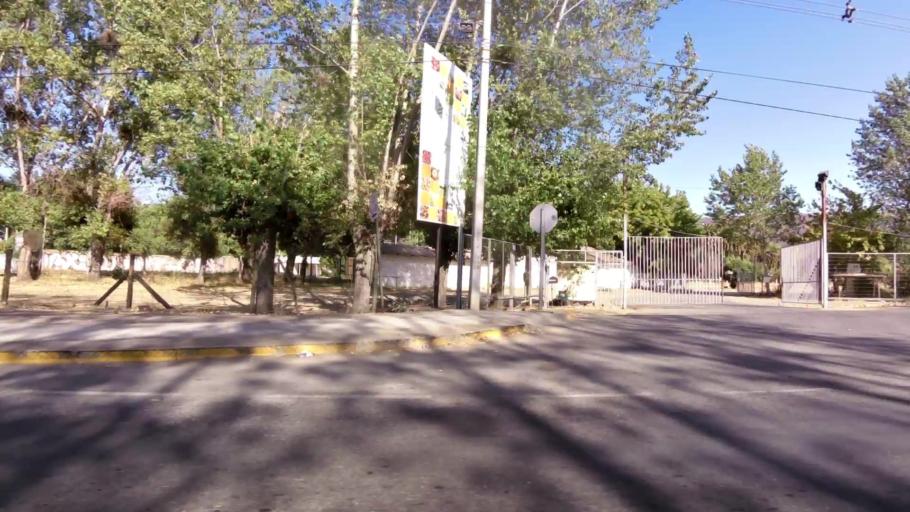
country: CL
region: Maule
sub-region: Provincia de Talca
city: Talca
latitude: -35.4202
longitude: -71.6755
